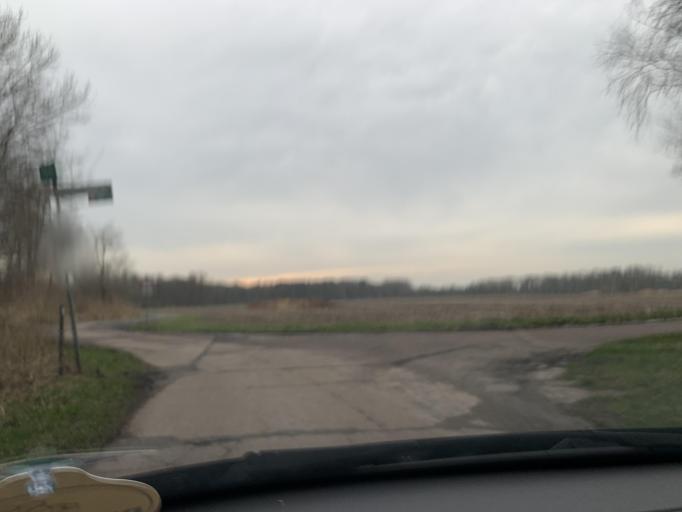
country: DE
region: Lower Saxony
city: Bad Zwischenahn
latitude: 53.2118
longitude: 7.9854
